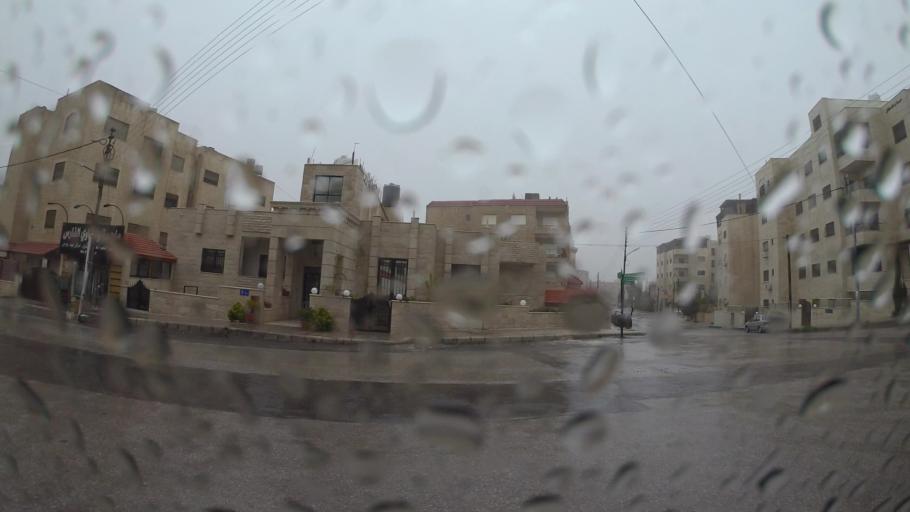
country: JO
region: Amman
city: Al Jubayhah
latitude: 32.0171
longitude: 35.8847
